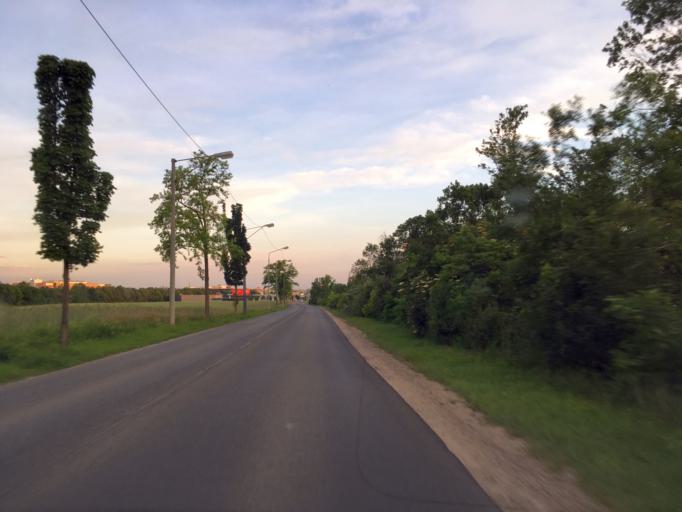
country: AT
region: Lower Austria
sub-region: Politischer Bezirk Wien-Umgebung
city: Gerasdorf bei Wien
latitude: 48.2718
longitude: 16.4568
